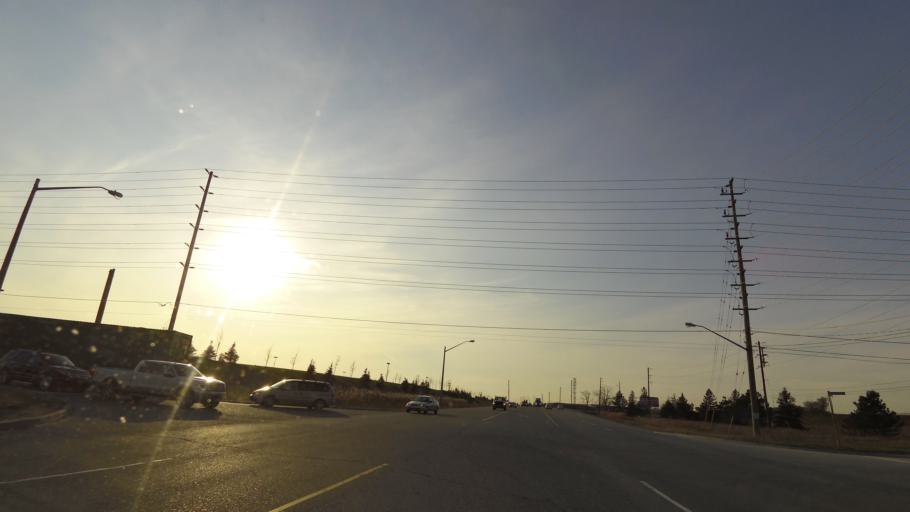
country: CA
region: Ontario
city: Vaughan
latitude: 43.8045
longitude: -79.6550
